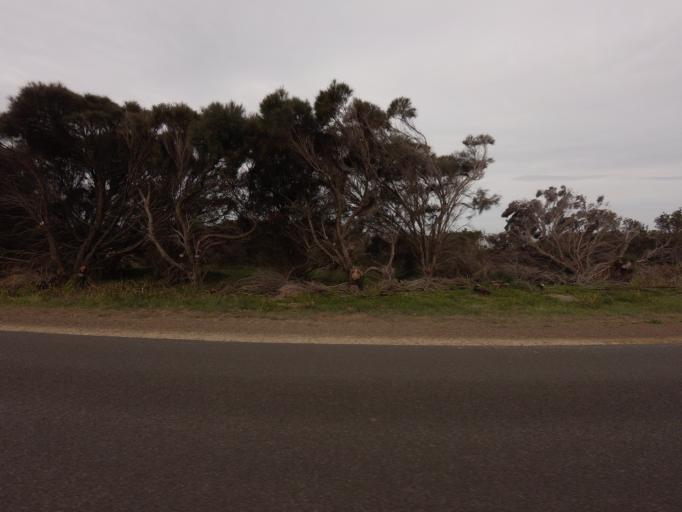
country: AU
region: Tasmania
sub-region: Sorell
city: Sorell
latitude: -42.2028
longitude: 148.0434
